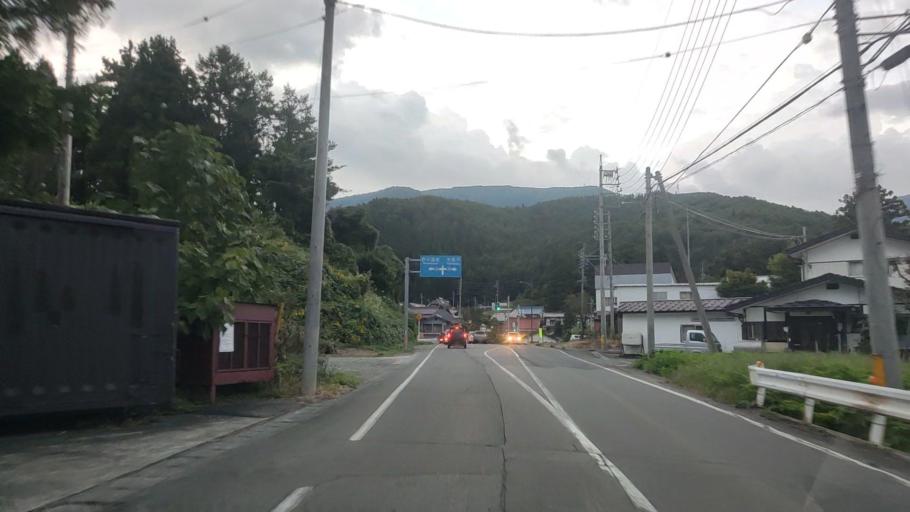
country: JP
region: Nagano
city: Iiyama
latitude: 36.8925
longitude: 138.4054
